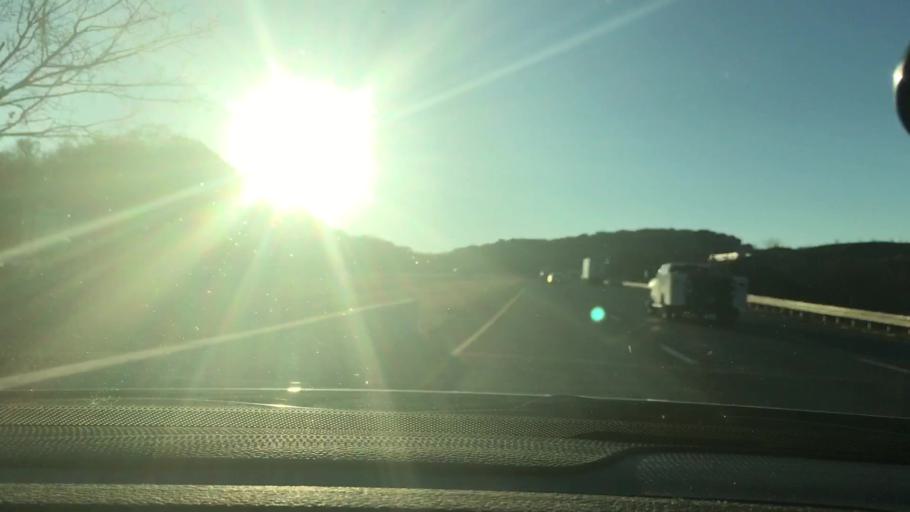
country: US
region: Oklahoma
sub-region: Murray County
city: Davis
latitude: 34.4473
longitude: -97.1323
